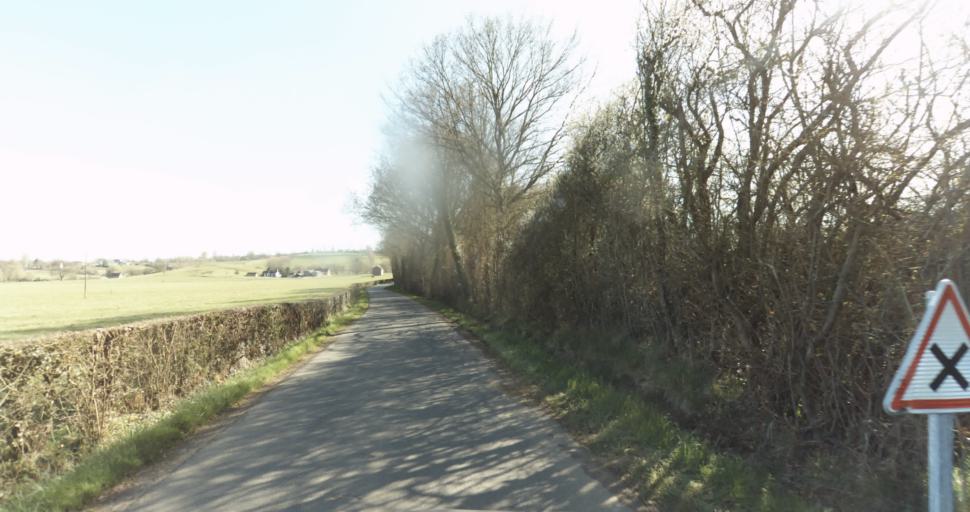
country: FR
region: Lower Normandy
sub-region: Departement du Calvados
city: Saint-Pierre-sur-Dives
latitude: 49.0277
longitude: 0.0559
